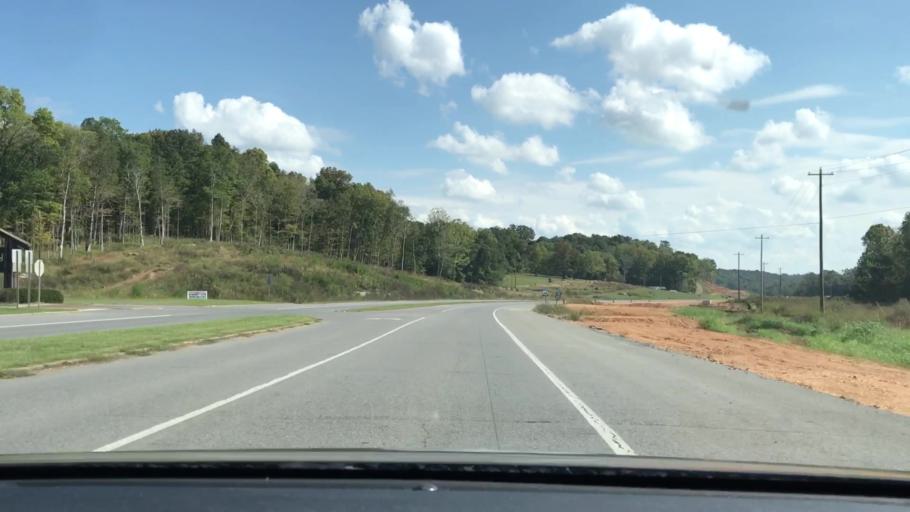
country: US
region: Kentucky
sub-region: Trigg County
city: Cadiz
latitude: 36.8054
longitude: -87.9275
